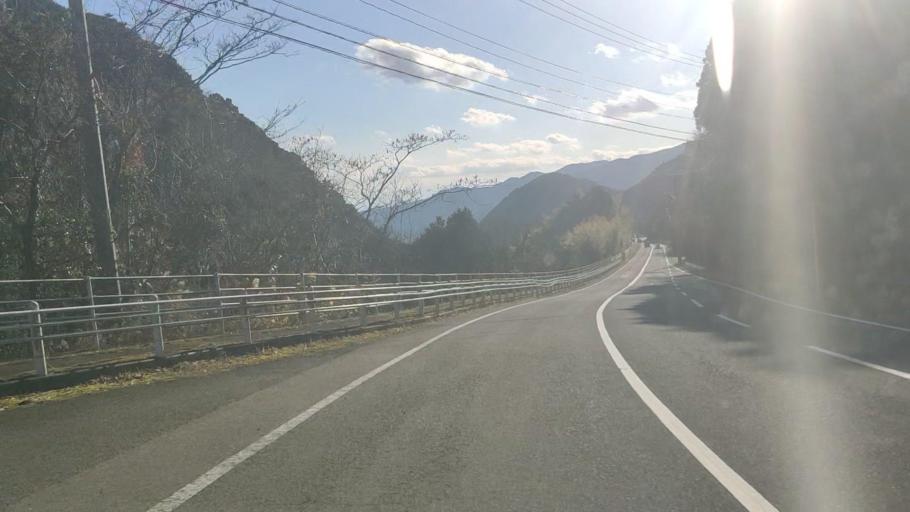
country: JP
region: Saga Prefecture
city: Kanzakimachi-kanzaki
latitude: 33.3850
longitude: 130.2608
